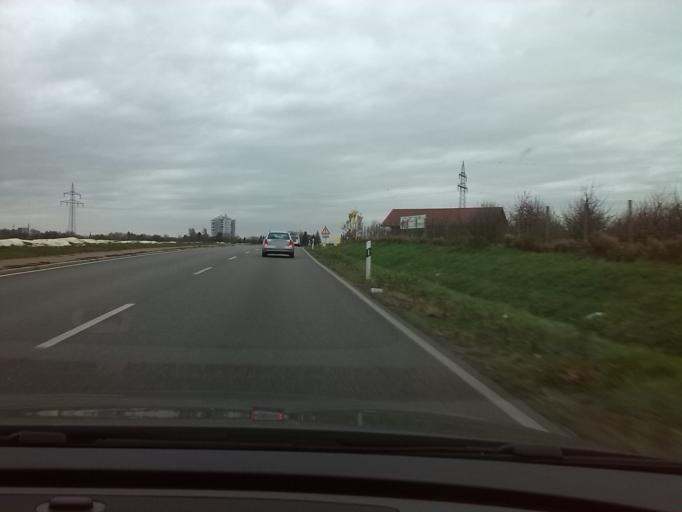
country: DE
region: Baden-Wuerttemberg
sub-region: Regierungsbezirk Stuttgart
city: Stuttgart Muehlhausen
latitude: 48.8229
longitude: 9.2474
